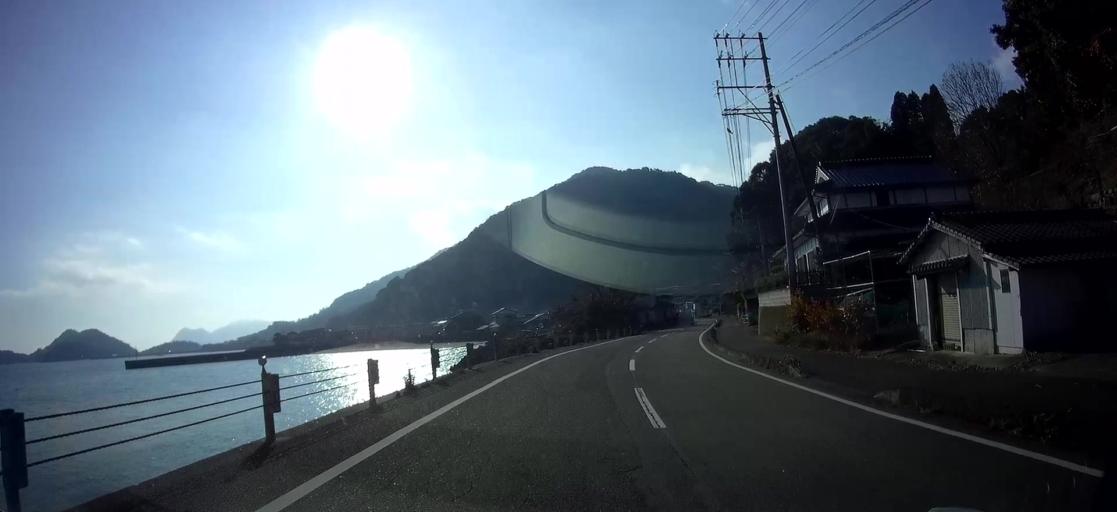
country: JP
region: Kumamoto
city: Minamata
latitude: 32.4100
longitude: 130.4072
